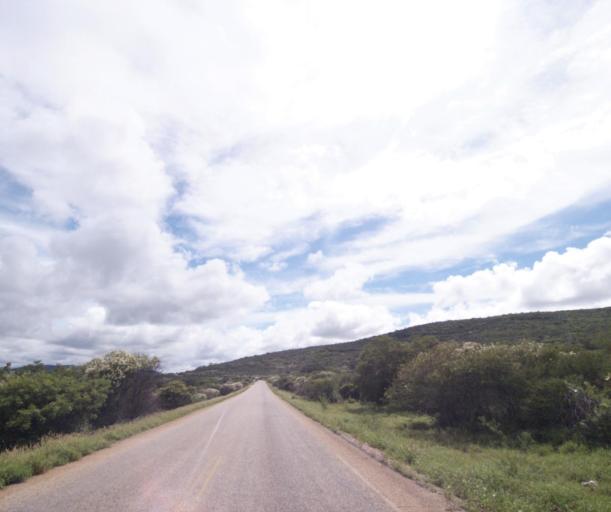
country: BR
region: Bahia
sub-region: Brumado
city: Brumado
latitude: -14.2066
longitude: -41.6235
